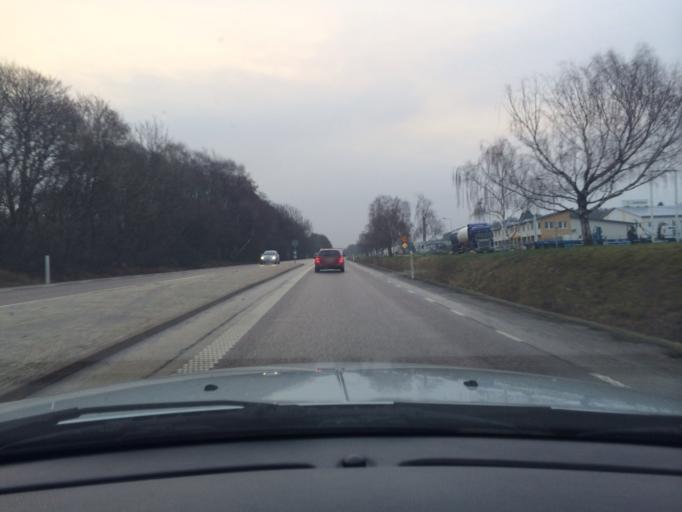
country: SE
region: Vaestra Goetaland
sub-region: Stenungsunds Kommun
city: Stenungsund
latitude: 58.0749
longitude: 11.8411
